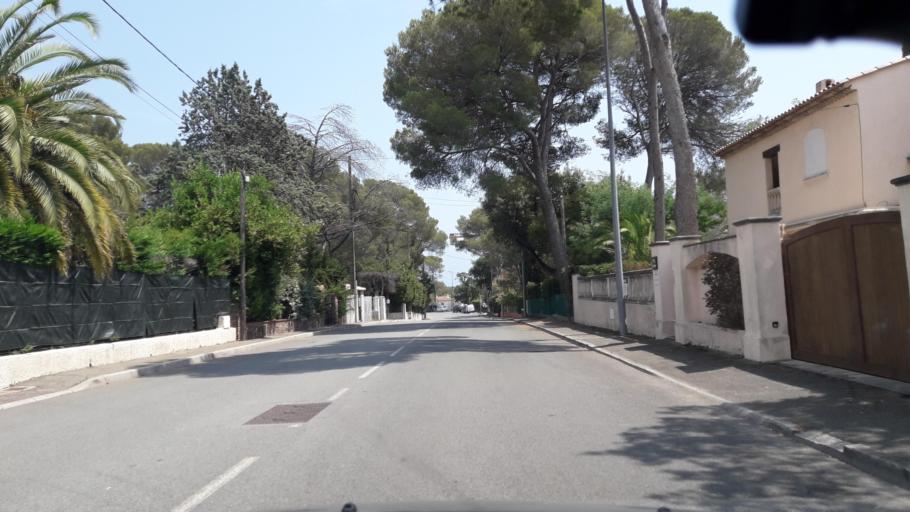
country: FR
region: Provence-Alpes-Cote d'Azur
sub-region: Departement du Var
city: Saint-Raphael
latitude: 43.4196
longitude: 6.7977
